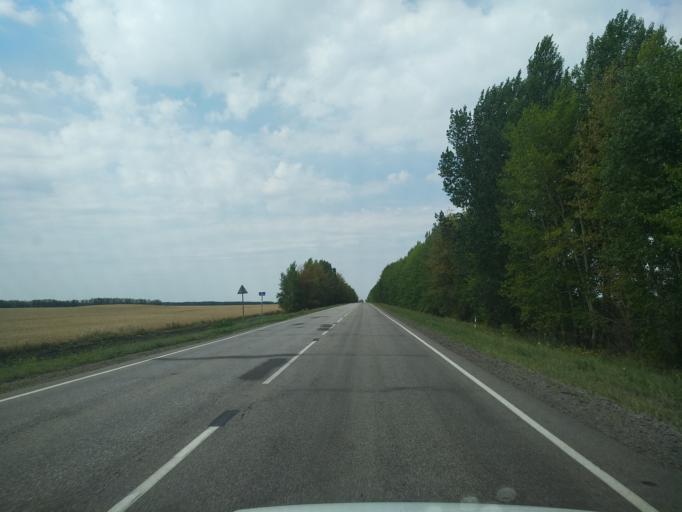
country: RU
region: Voronezj
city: Pereleshino
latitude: 51.7218
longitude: 40.0325
